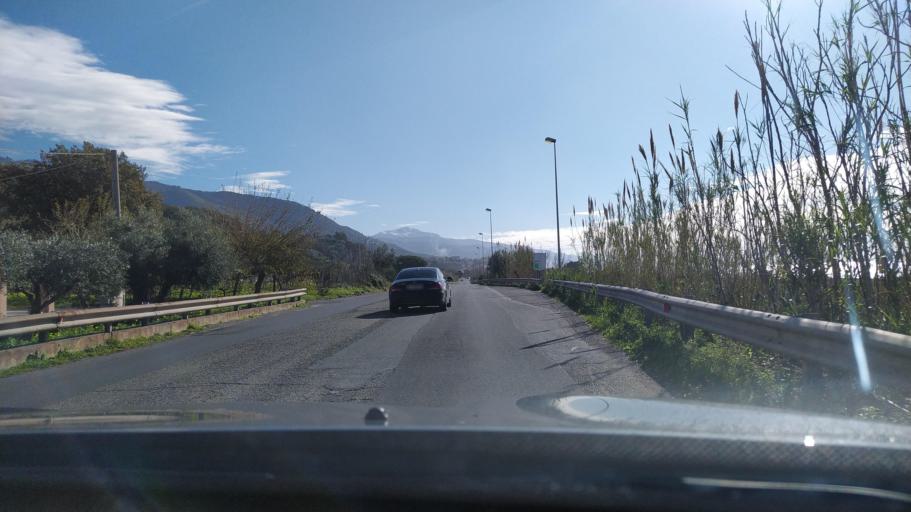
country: IT
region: Calabria
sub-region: Provincia di Cosenza
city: Scarcelli
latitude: 39.3846
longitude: 16.0219
